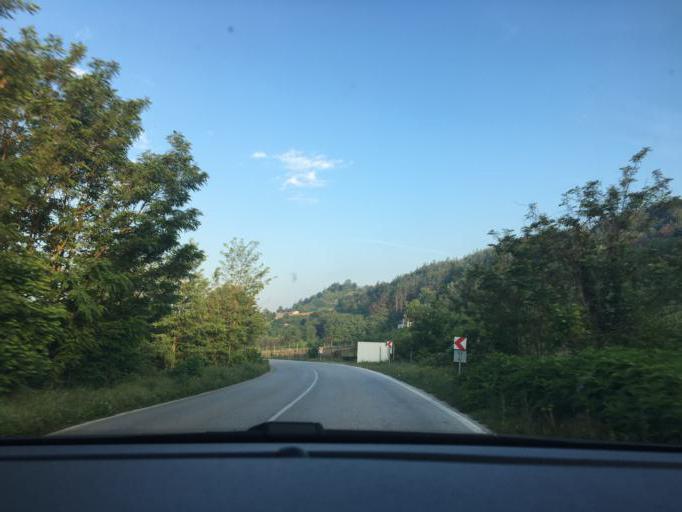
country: MK
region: Novo Selo
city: Novo Selo
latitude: 41.3984
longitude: 22.9845
